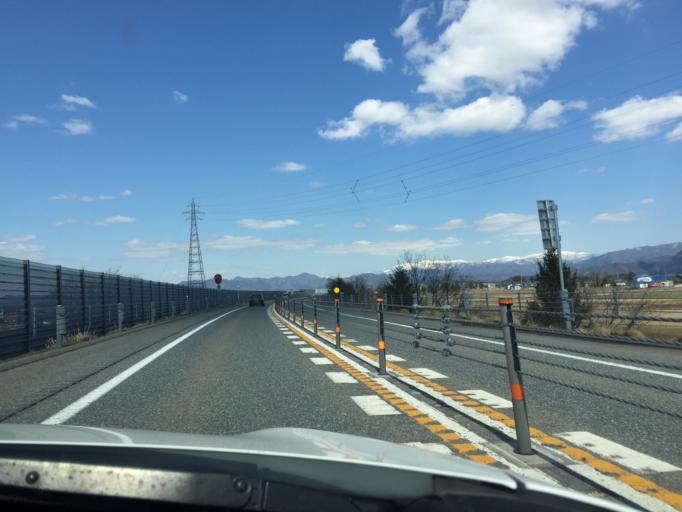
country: JP
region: Yamagata
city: Yonezawa
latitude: 37.9672
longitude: 140.1232
